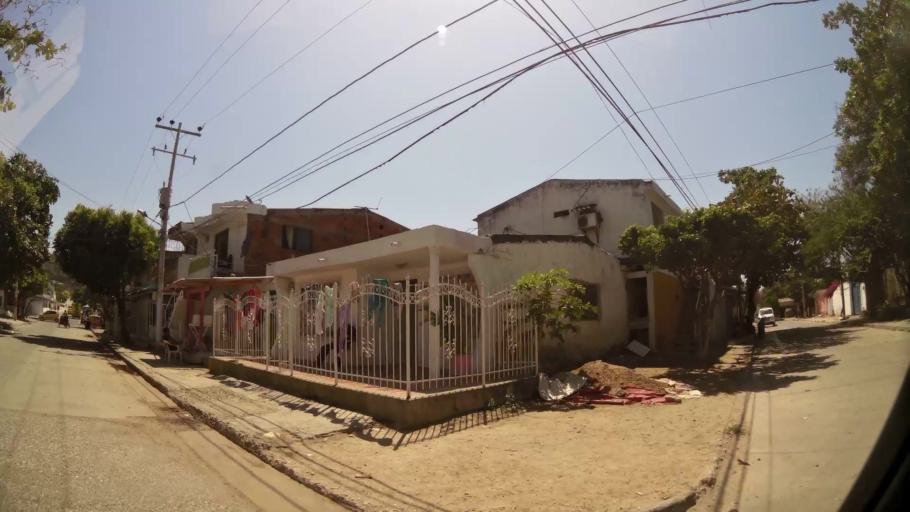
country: CO
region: Bolivar
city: Cartagena
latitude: 10.4338
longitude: -75.5307
